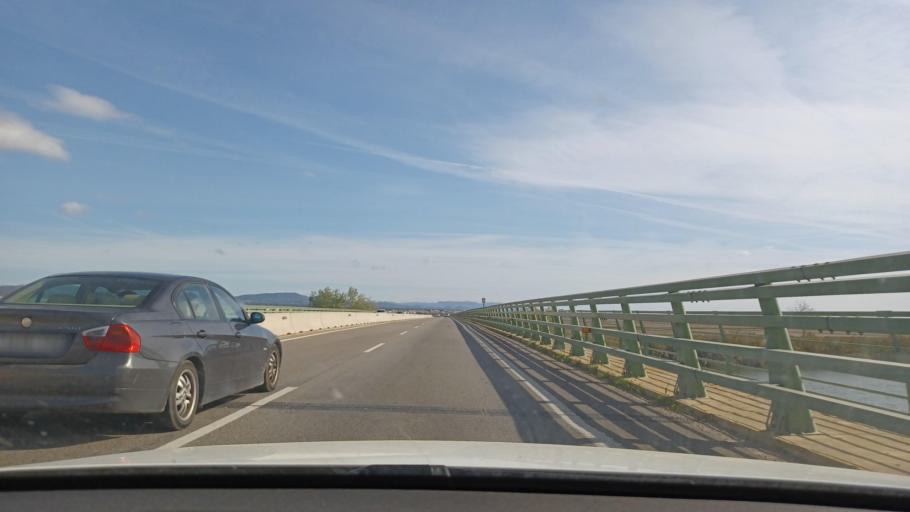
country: ES
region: Catalonia
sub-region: Provincia de Tarragona
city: Amposta
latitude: 40.7095
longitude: 0.5899
